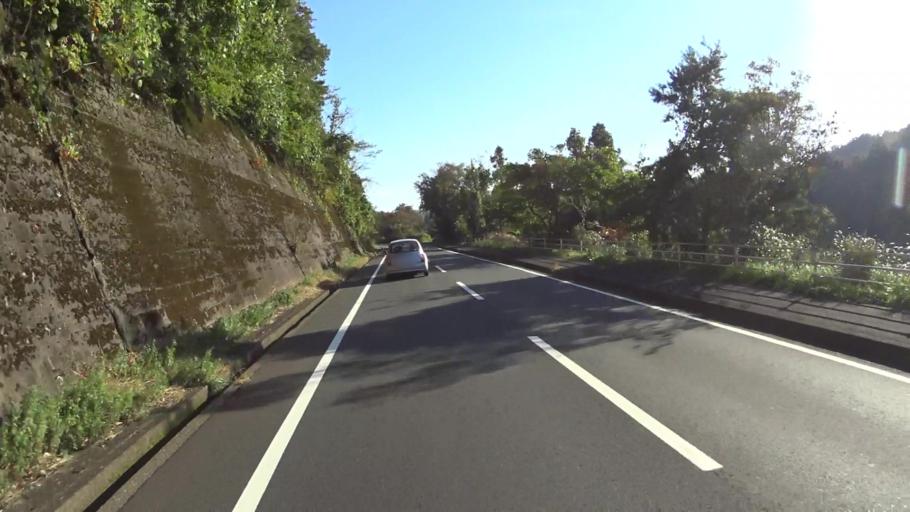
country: JP
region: Kyoto
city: Fukuchiyama
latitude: 35.3855
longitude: 135.0964
